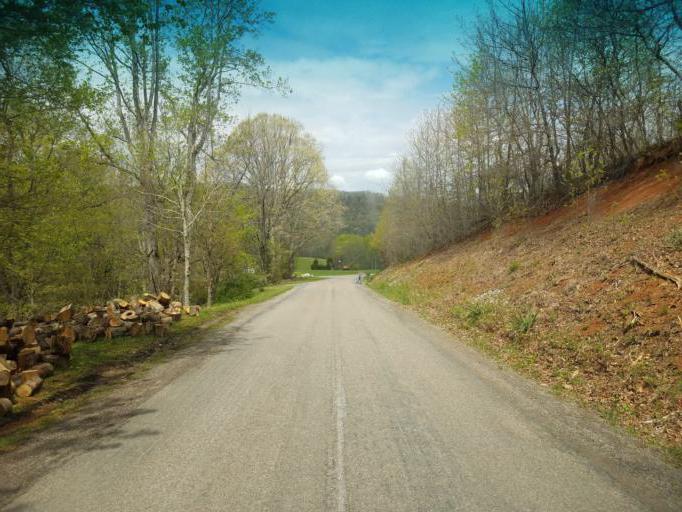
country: US
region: Virginia
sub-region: Smyth County
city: Marion
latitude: 36.8011
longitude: -81.4625
